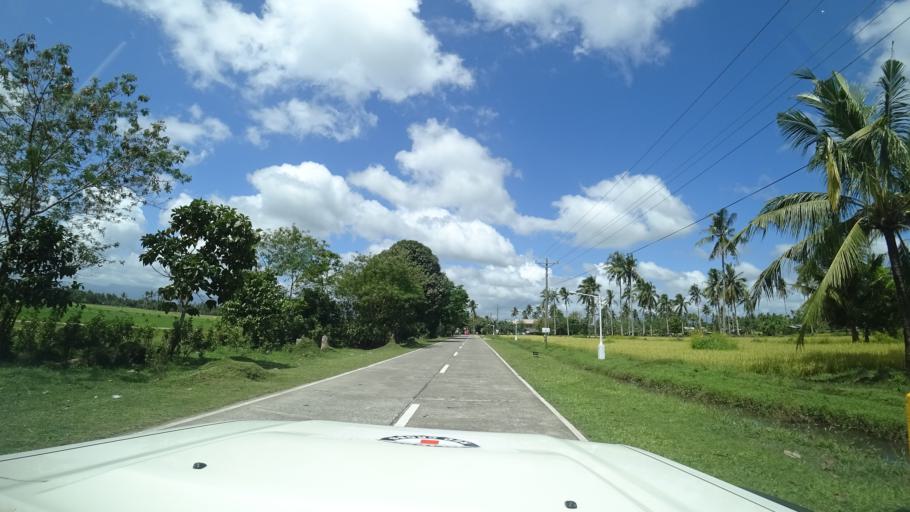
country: PH
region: Eastern Visayas
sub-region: Province of Leyte
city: Mayorga
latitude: 10.9039
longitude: 124.9889
